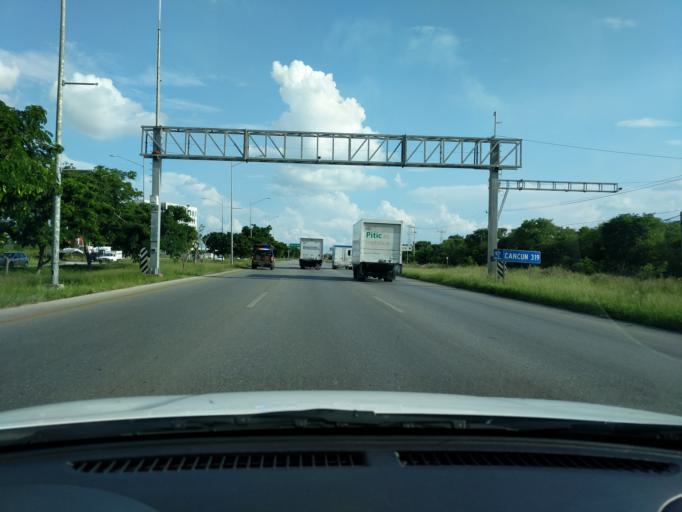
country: MX
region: Yucatan
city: Itzincab Palomeque
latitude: 20.9438
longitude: -89.6996
